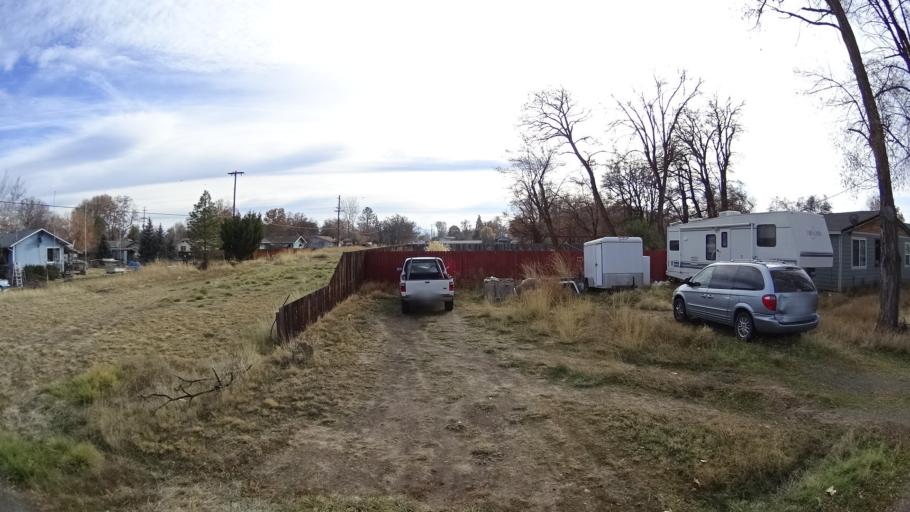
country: US
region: California
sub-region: Siskiyou County
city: Montague
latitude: 41.7318
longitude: -122.5333
